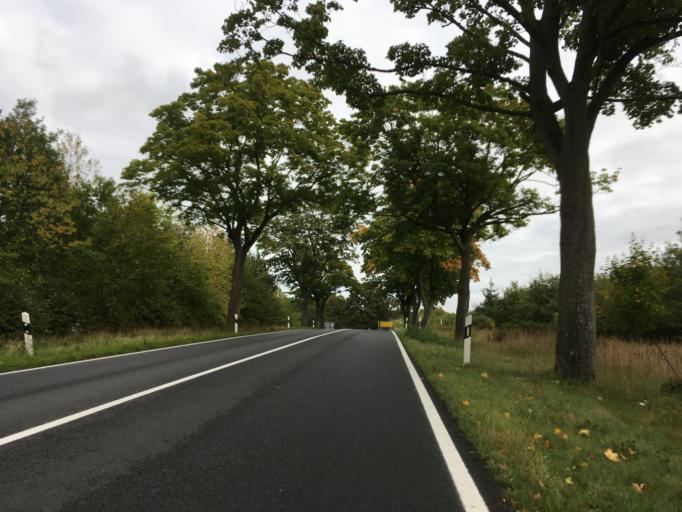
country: DE
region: Brandenburg
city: Werftpfuhl
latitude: 52.7009
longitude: 13.8730
